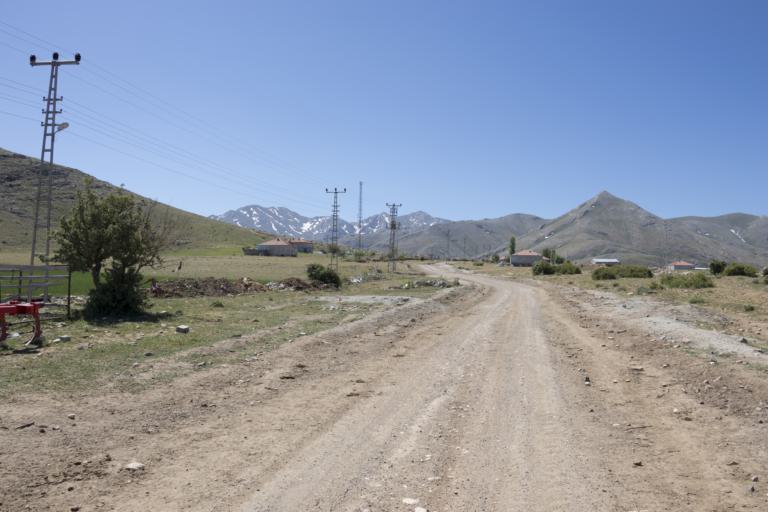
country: TR
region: Kayseri
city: Toklar
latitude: 38.4157
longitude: 36.0954
